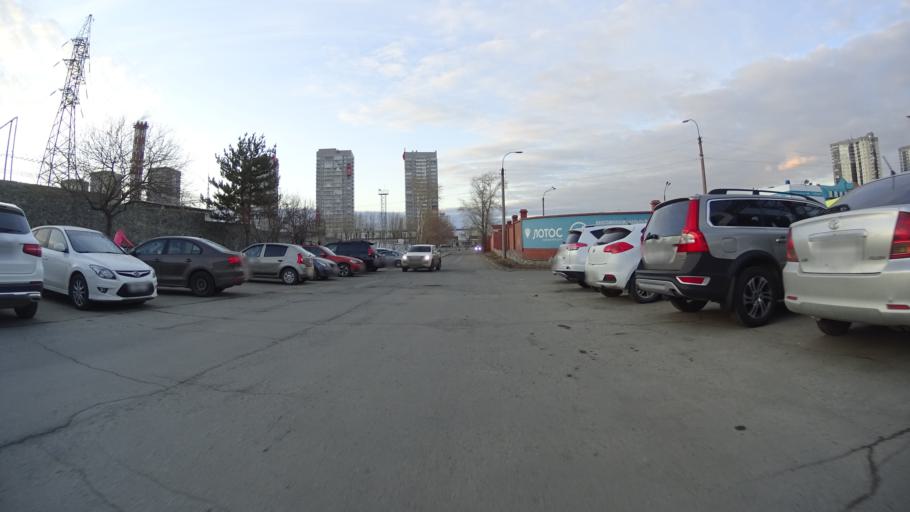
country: RU
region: Chelyabinsk
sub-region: Gorod Chelyabinsk
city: Chelyabinsk
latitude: 55.1688
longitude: 61.3702
